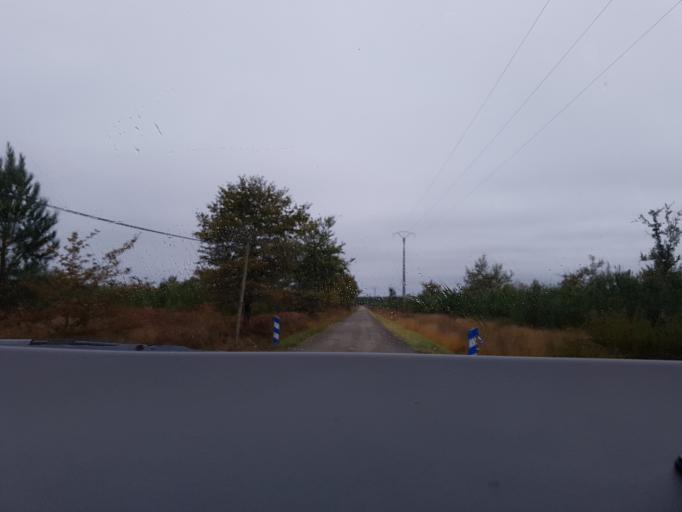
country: FR
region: Aquitaine
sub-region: Departement des Landes
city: Roquefort
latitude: 44.1293
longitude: -0.4156
